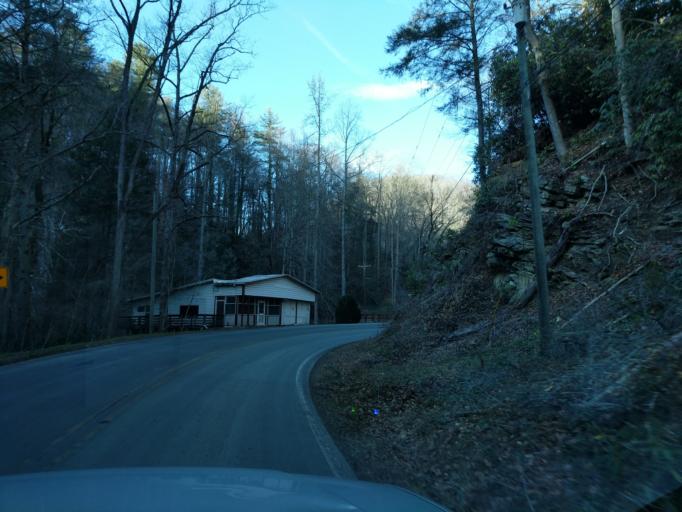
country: US
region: North Carolina
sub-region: Henderson County
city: Edneyville
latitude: 35.4540
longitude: -82.2978
